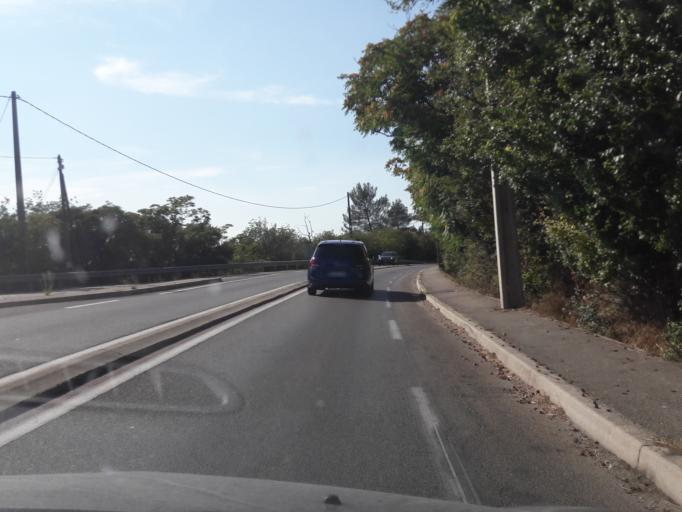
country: FR
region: Provence-Alpes-Cote d'Azur
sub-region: Departement des Bouches-du-Rhone
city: Bouc-Bel-Air
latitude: 43.4777
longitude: 5.4268
